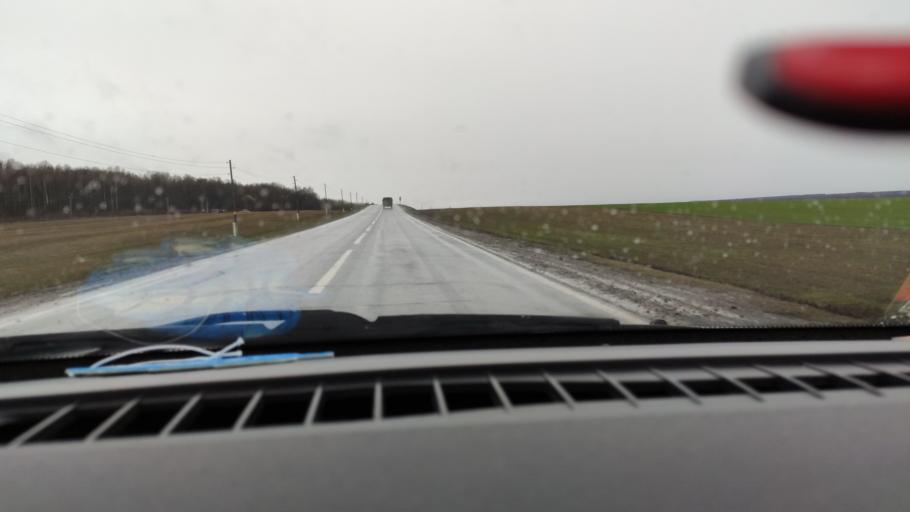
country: RU
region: Tatarstan
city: Nurlat
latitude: 54.6279
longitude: 50.9515
